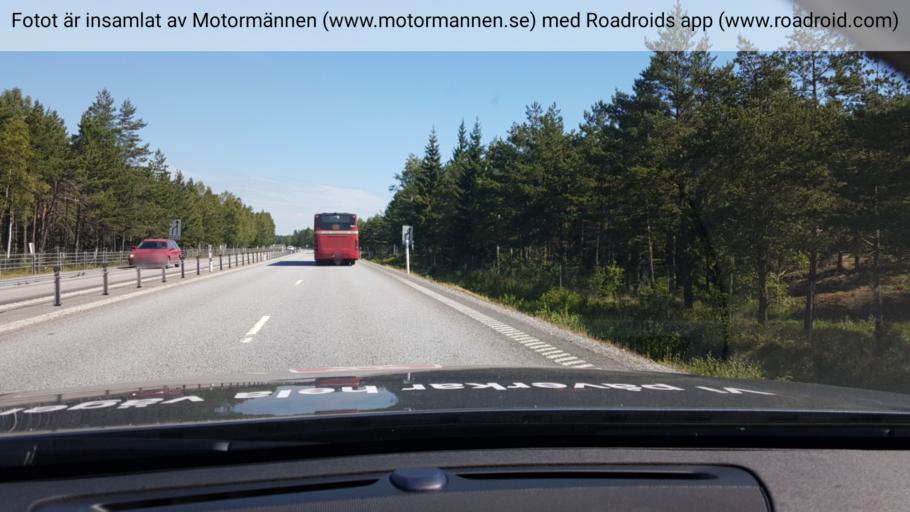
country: SE
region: Stockholm
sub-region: Osterakers Kommun
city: Akersberga
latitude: 59.5980
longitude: 18.2725
